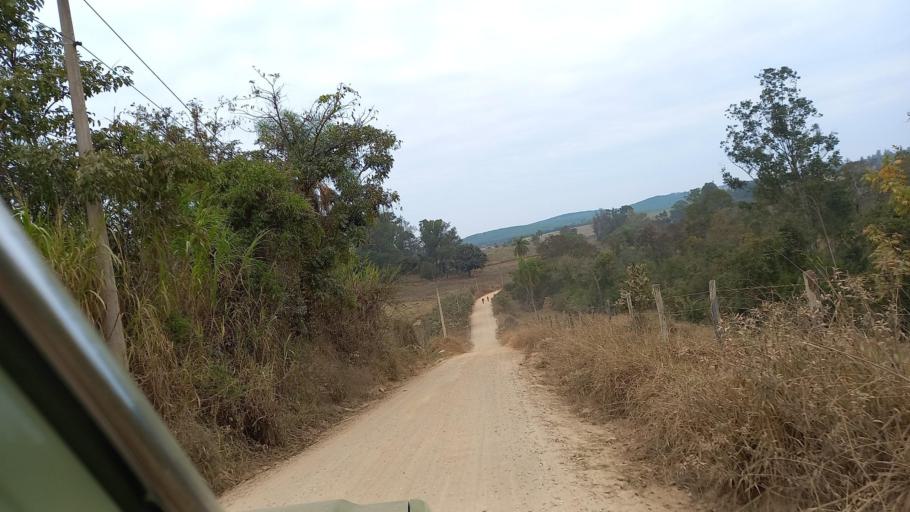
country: BR
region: Sao Paulo
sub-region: Moji-Guacu
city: Mogi-Gaucu
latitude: -22.3029
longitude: -46.8322
